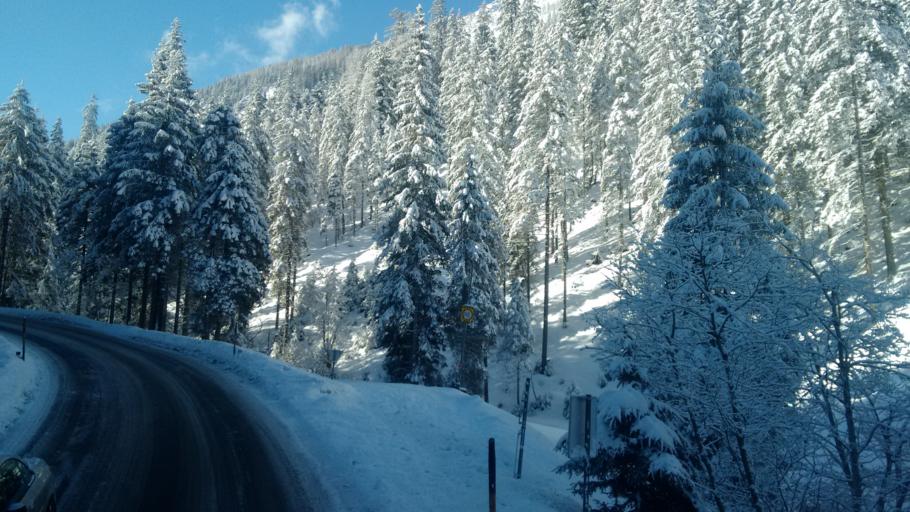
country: AT
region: Salzburg
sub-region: Politischer Bezirk Sankt Johann im Pongau
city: Radstadt
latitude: 47.3374
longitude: 13.4390
